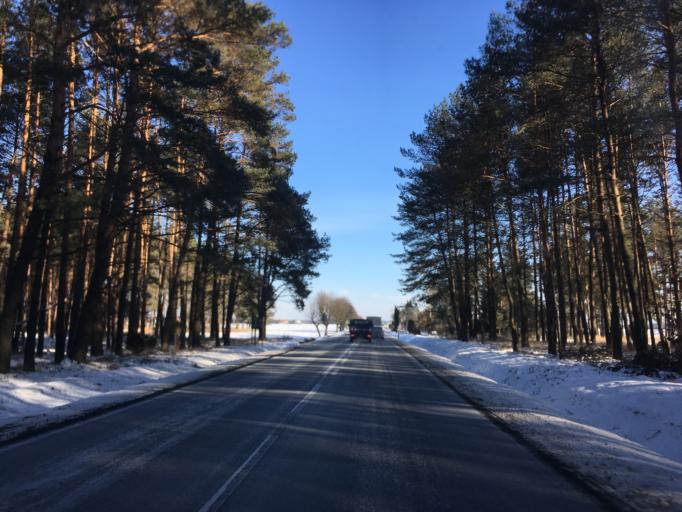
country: PL
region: Pomeranian Voivodeship
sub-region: Powiat koscierski
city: Lipusz
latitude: 54.1336
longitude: 17.8372
